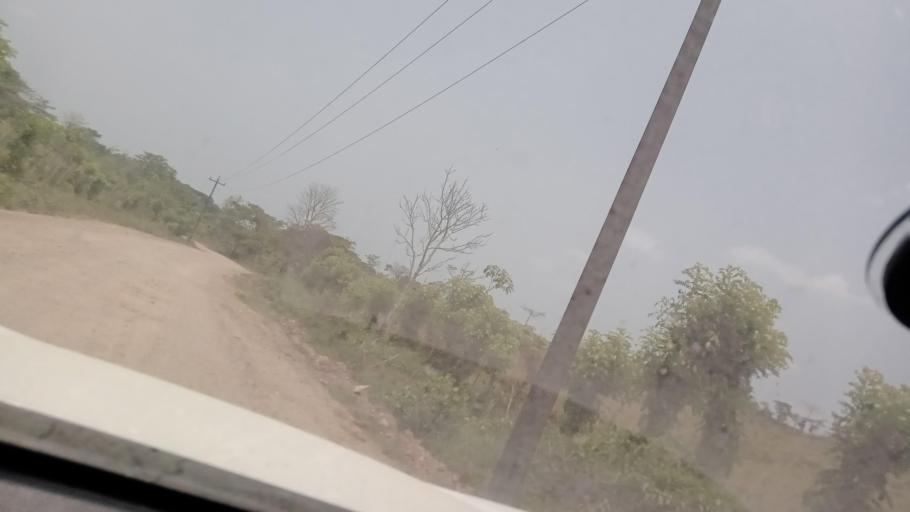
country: MX
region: Chiapas
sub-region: Tecpatan
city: Raudales Malpaso
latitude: 17.4221
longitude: -93.7919
